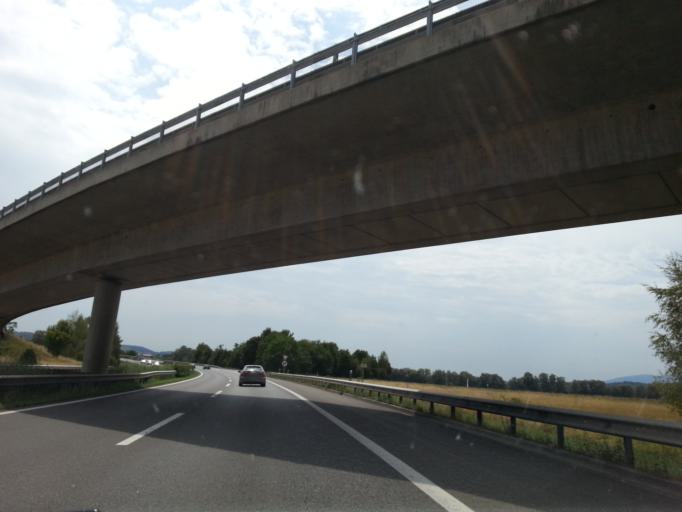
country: CH
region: Vaud
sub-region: Jura-Nord vaudois District
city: Chavornay
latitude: 46.7279
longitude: 6.5700
